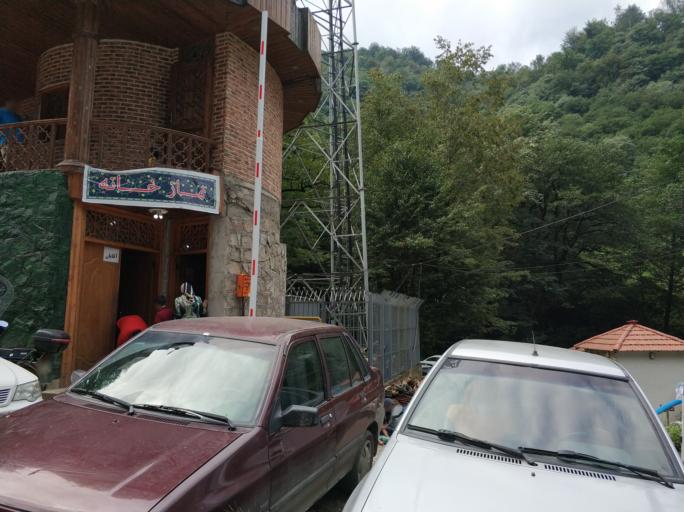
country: IR
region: Gilan
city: Fuman
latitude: 37.0732
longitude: 49.2492
